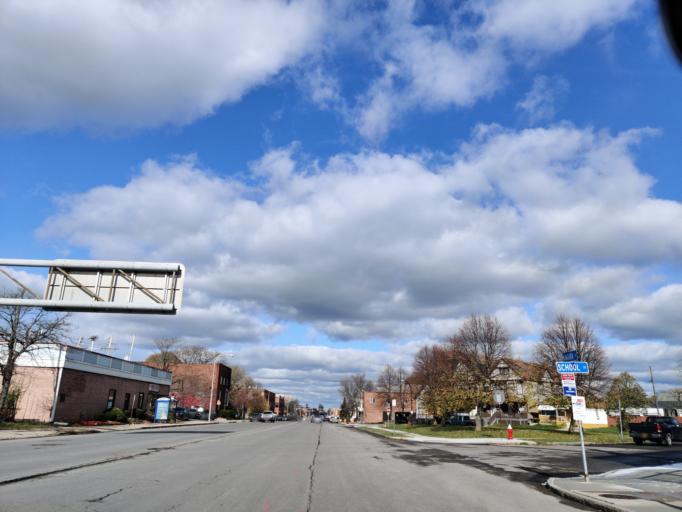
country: US
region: New York
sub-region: Erie County
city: Buffalo
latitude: 42.9103
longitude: -78.9000
